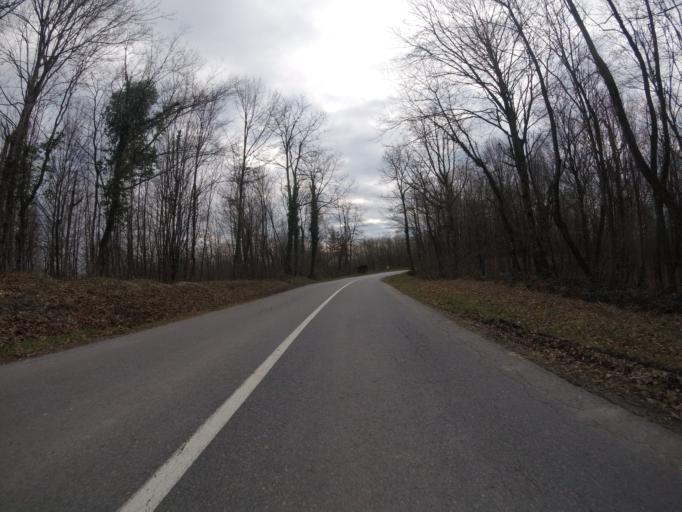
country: HR
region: Zagrebacka
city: Mraclin
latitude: 45.5449
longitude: 16.0601
